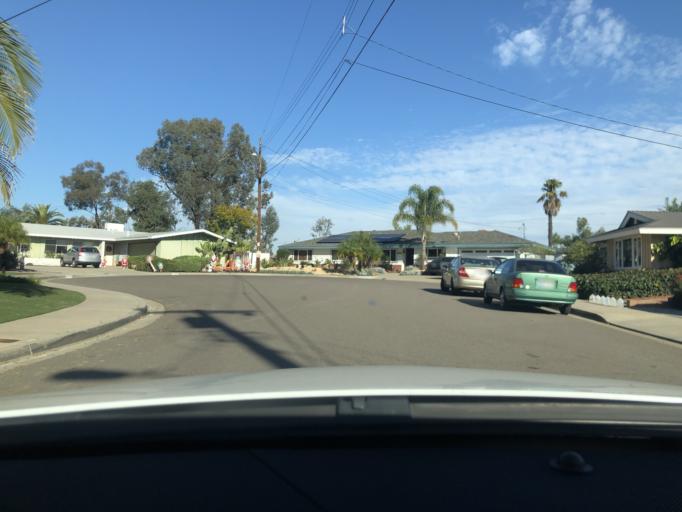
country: US
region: California
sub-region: San Diego County
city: Lemon Grove
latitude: 32.7529
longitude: -117.0688
